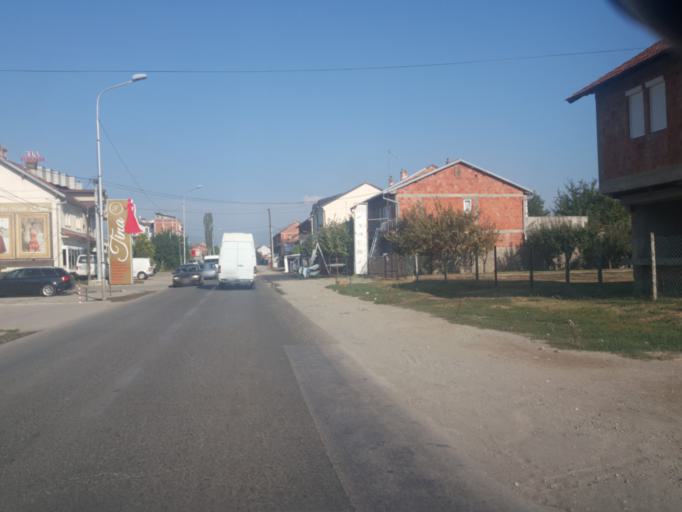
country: XK
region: Gjakova
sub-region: Komuna e Gjakoves
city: Gjakove
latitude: 42.3996
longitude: 20.4168
